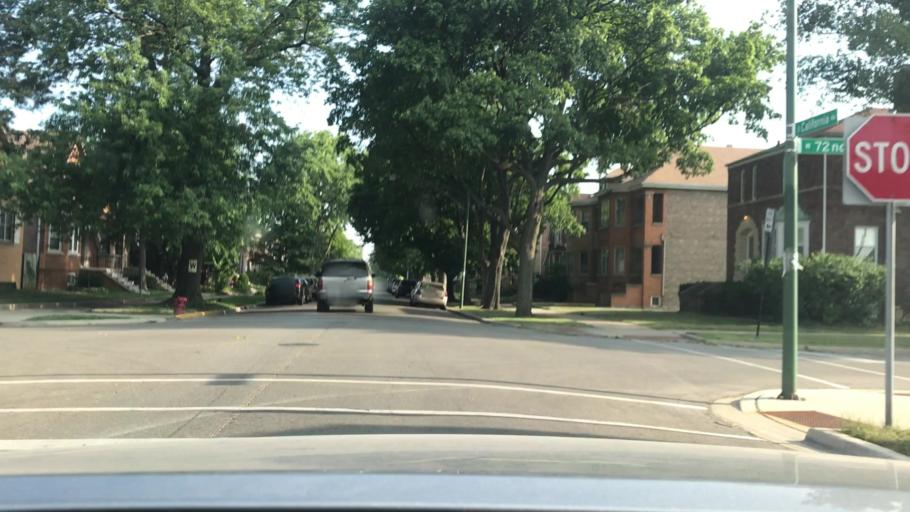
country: US
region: Illinois
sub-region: Cook County
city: Evergreen Park
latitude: 41.7626
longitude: -87.6930
